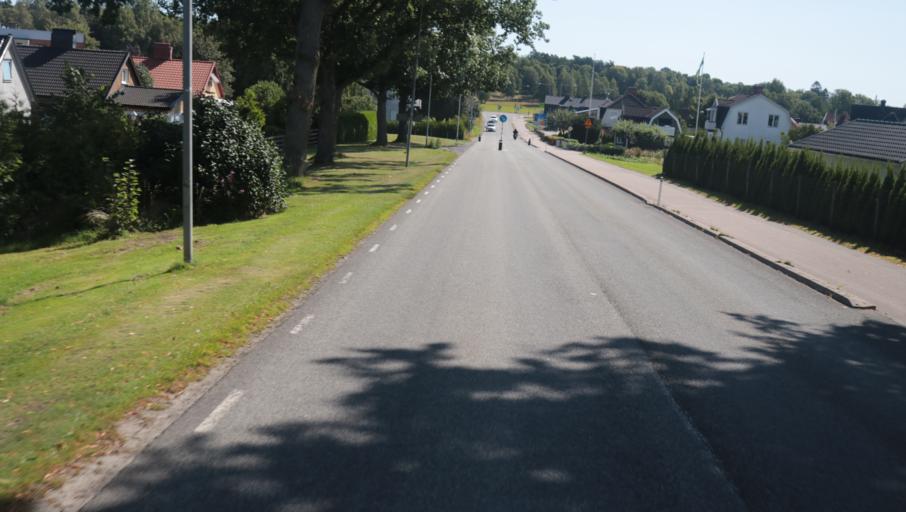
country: SE
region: Blekinge
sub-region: Karlshamns Kommun
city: Karlshamn
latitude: 56.2005
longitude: 14.8311
